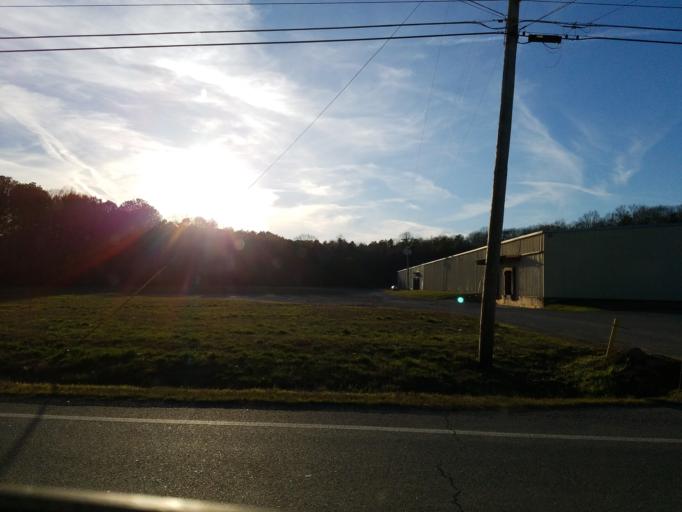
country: US
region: Georgia
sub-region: Gordon County
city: Calhoun
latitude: 34.5977
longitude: -84.9470
